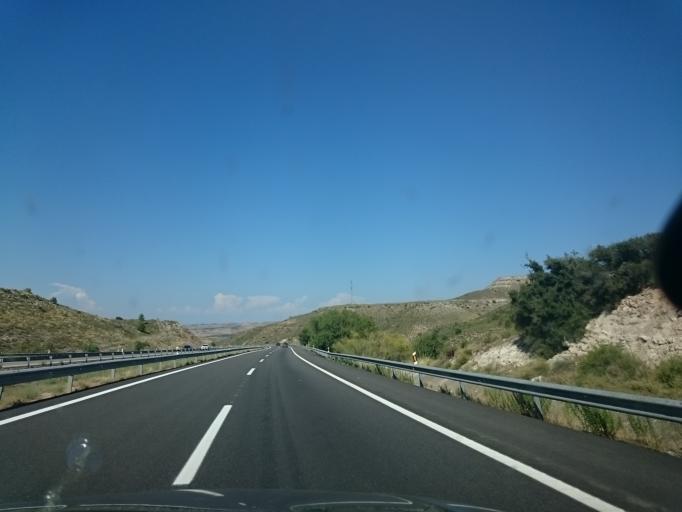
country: ES
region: Aragon
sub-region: Provincia de Huesca
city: Fraga
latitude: 41.4713
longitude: 0.3081
